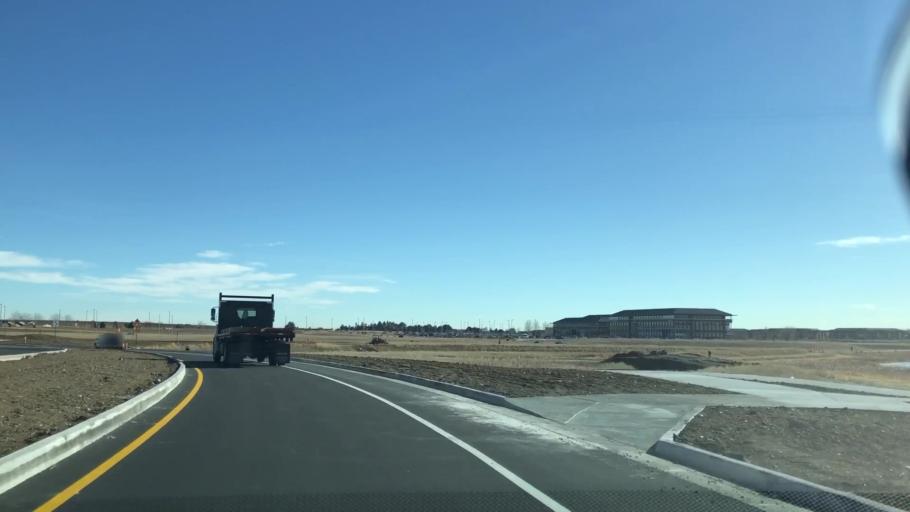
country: US
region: Colorado
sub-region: Larimer County
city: Loveland
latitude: 40.4268
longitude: -105.0078
